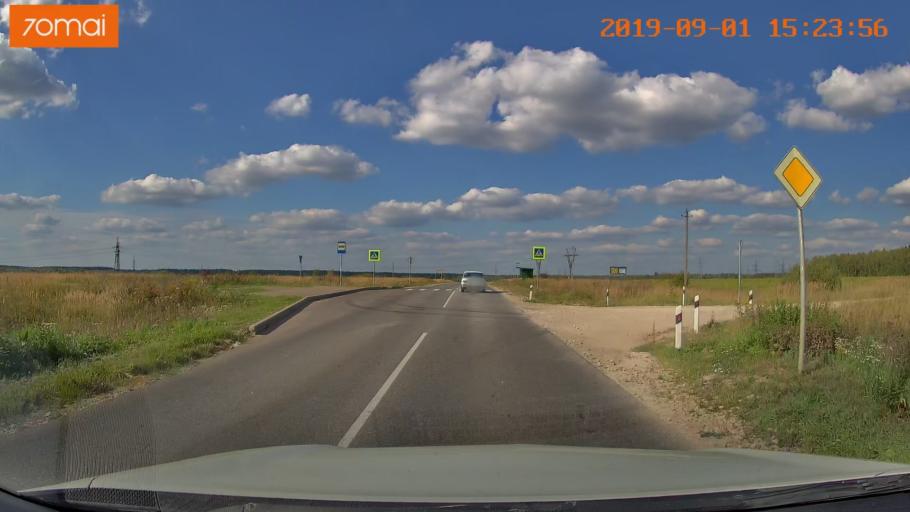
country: RU
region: Kaluga
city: Maloyaroslavets
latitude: 54.9491
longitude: 36.4585
